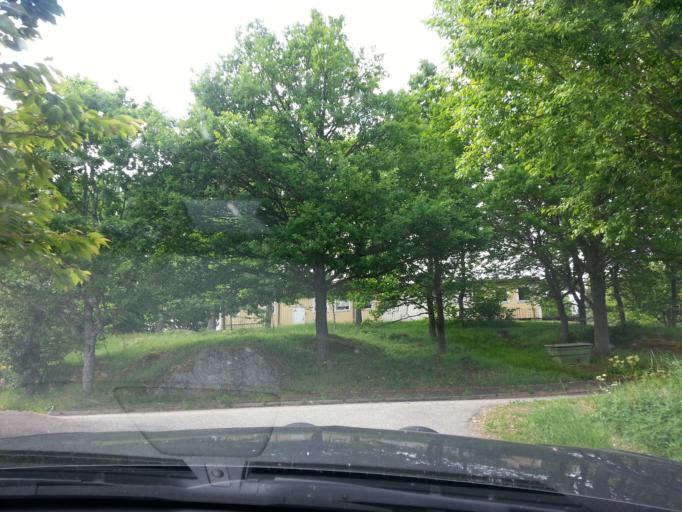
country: SE
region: Joenkoeping
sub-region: Vetlanda Kommun
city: Vetlanda
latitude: 57.2975
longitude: 15.1304
